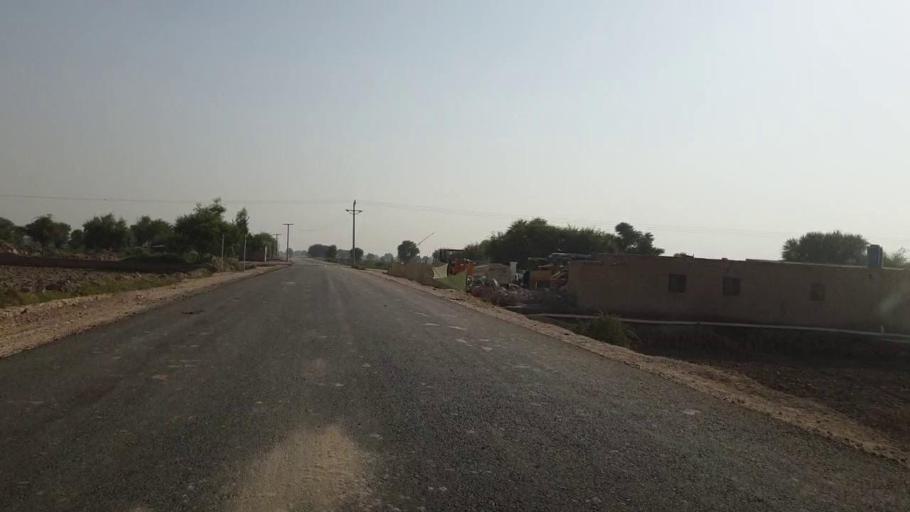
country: PK
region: Sindh
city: Bhan
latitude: 26.5345
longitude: 67.7884
